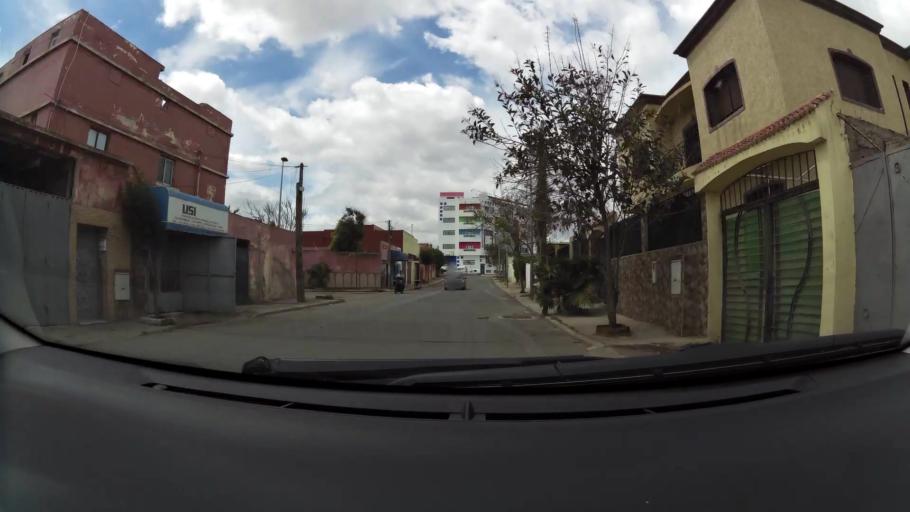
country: MA
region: Grand Casablanca
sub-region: Casablanca
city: Casablanca
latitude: 33.6149
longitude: -7.5453
